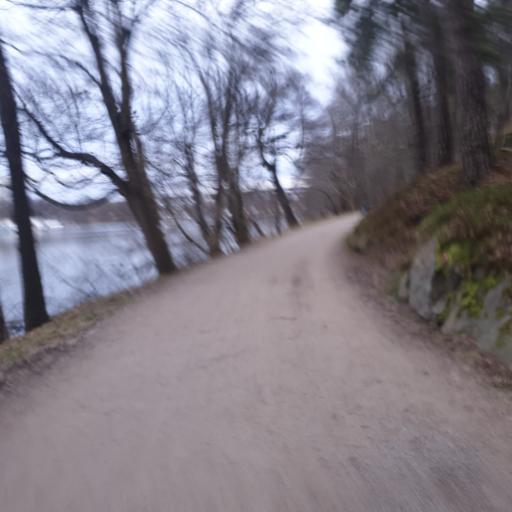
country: SE
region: Stockholm
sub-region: Stockholms Kommun
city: Arsta
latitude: 59.3026
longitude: 18.0634
